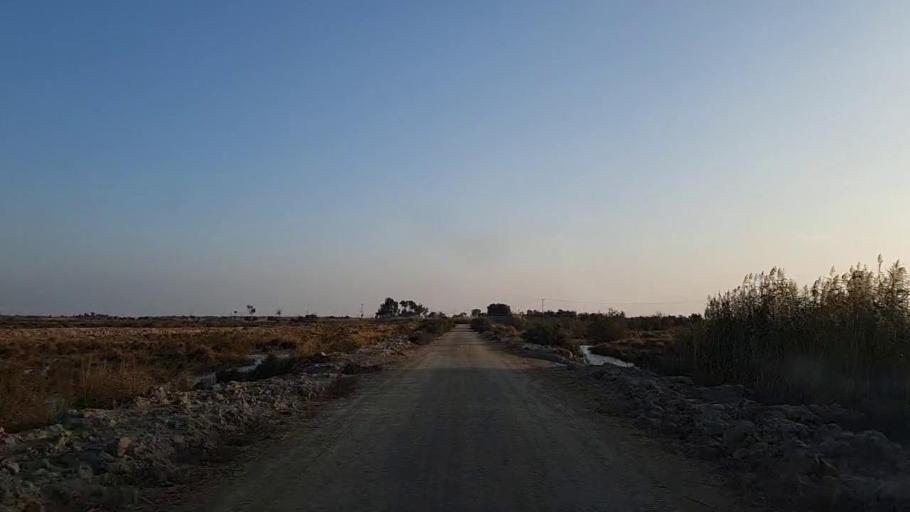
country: PK
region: Sindh
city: Sanghar
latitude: 26.2591
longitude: 68.9779
